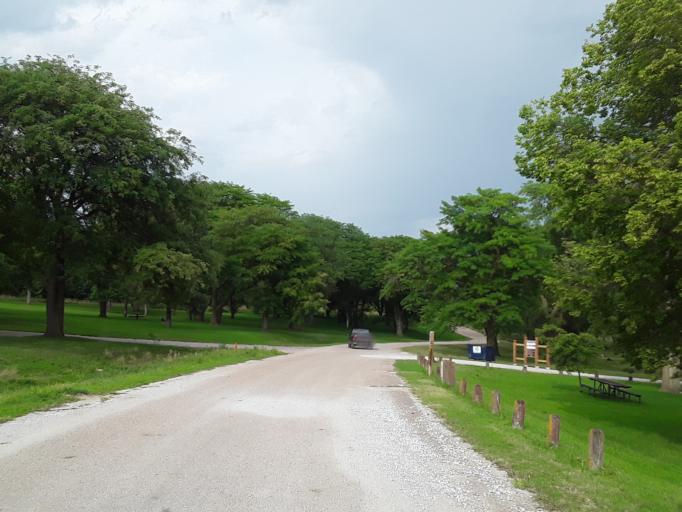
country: US
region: Nebraska
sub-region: Saunders County
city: Ashland
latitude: 41.1023
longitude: -96.4419
